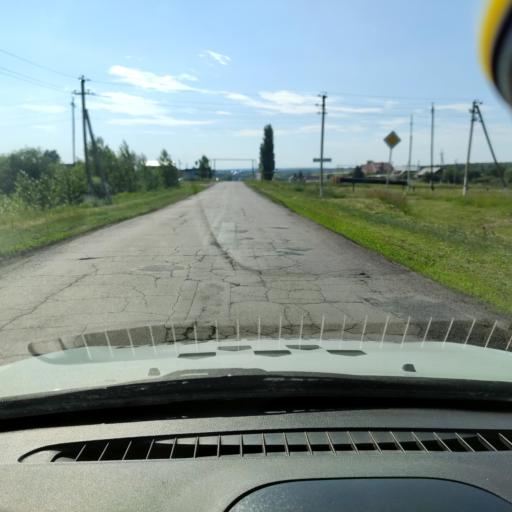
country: RU
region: Samara
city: Tol'yatti
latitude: 53.3543
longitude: 49.3208
